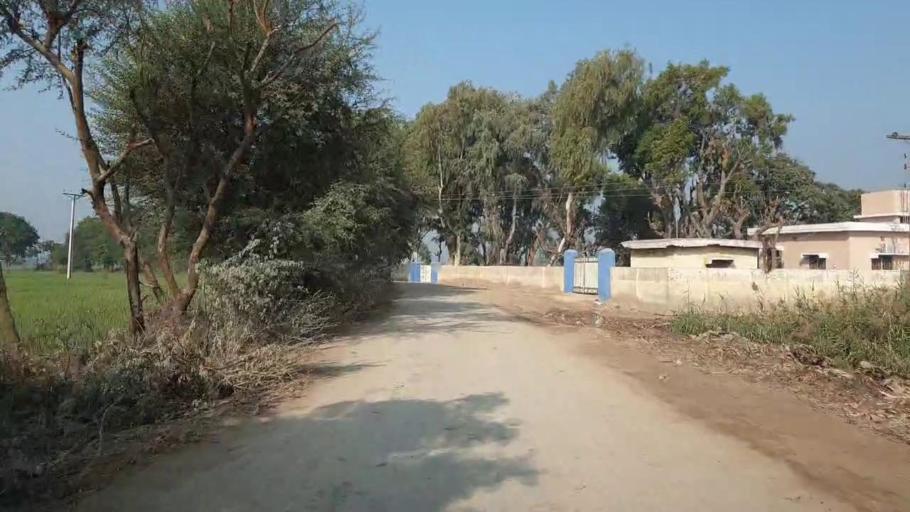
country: PK
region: Sindh
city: Matiari
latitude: 25.6765
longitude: 68.4988
